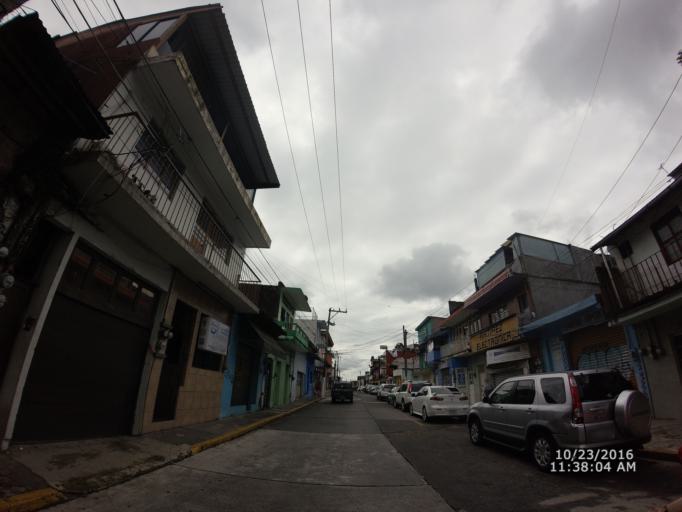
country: MX
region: Veracruz
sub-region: Xalapa
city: Xalapa de Enriquez
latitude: 19.5336
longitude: -96.9270
